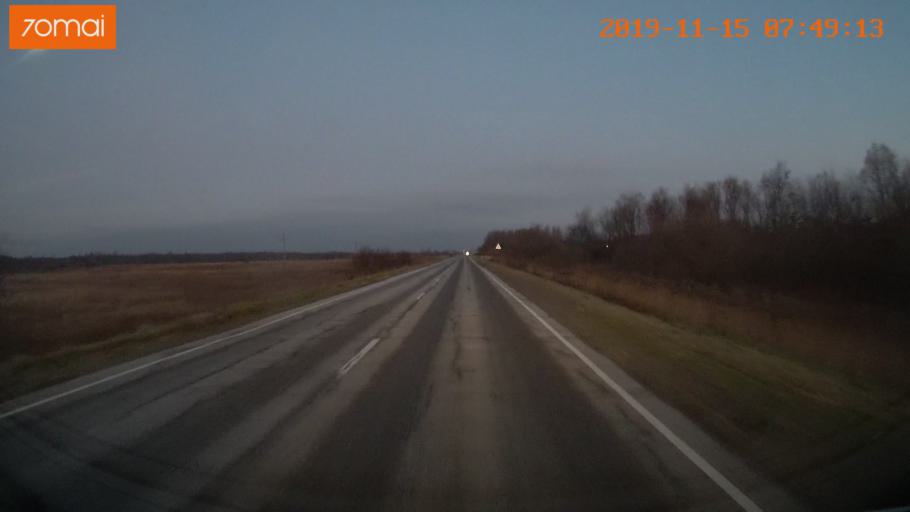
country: RU
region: Vologda
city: Cherepovets
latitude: 58.8588
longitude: 38.2330
